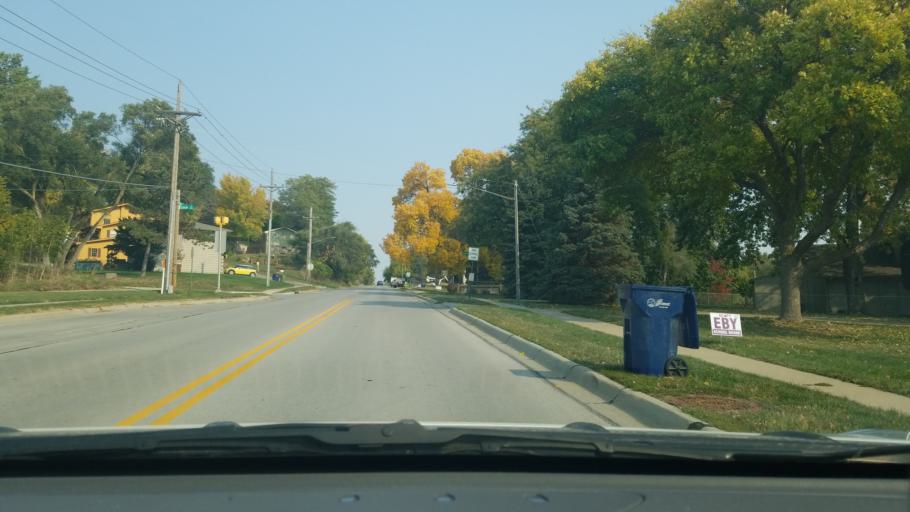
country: US
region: Nebraska
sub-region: Sarpy County
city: Bellevue
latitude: 41.1548
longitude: -95.9090
